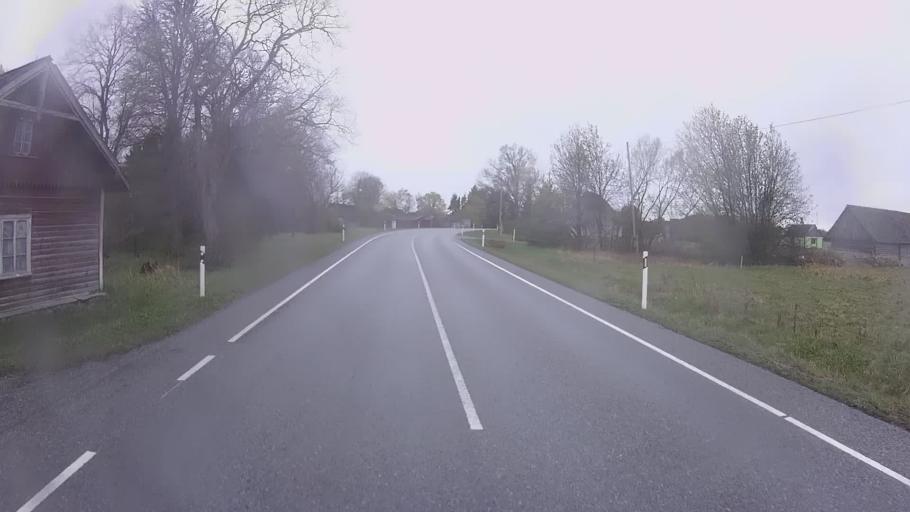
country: EE
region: Hiiumaa
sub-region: Kaerdla linn
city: Kardla
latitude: 58.9958
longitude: 22.5282
